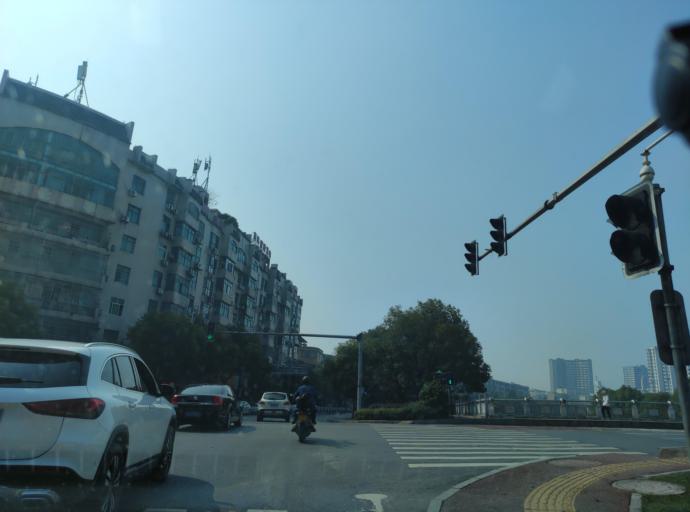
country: CN
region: Jiangxi Sheng
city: Pingxiang
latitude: 27.6374
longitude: 113.8540
